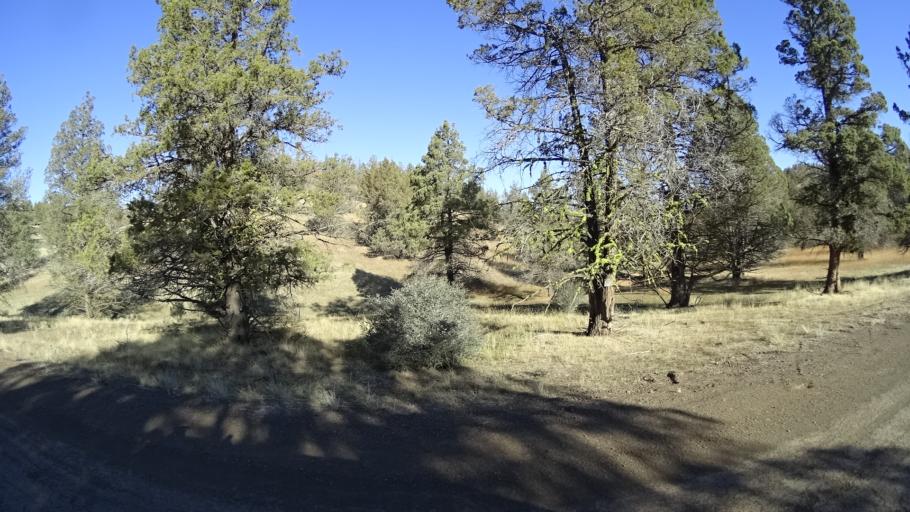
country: US
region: California
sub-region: Siskiyou County
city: Montague
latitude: 41.9164
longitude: -122.4245
